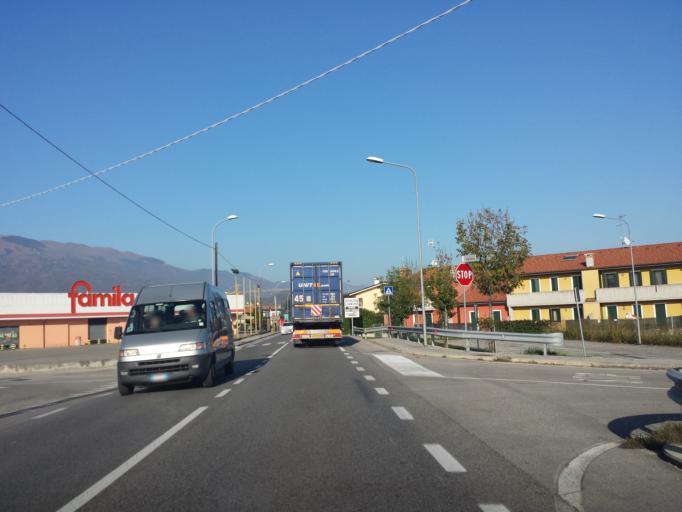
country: IT
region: Veneto
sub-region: Provincia di Treviso
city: Bigolino
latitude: 45.8518
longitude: 12.0231
